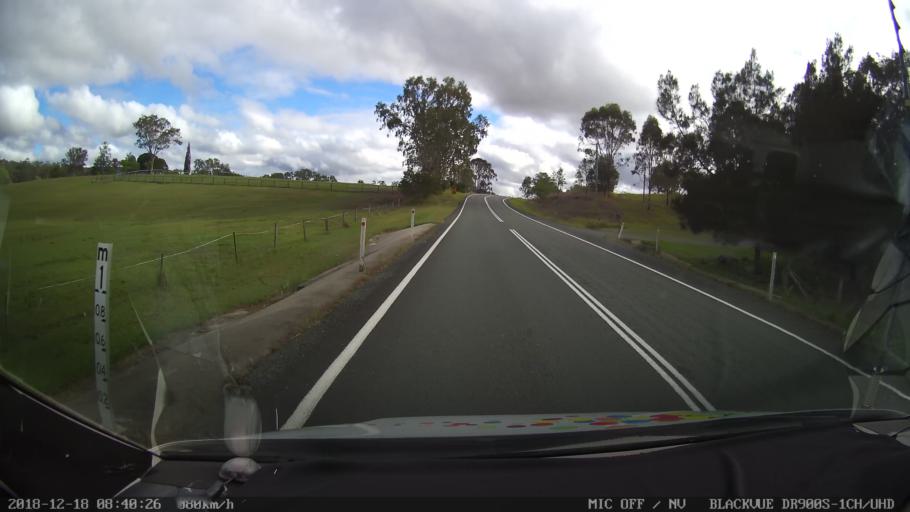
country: AU
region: Queensland
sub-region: Logan
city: Cedar Vale
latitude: -28.2422
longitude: 152.8471
